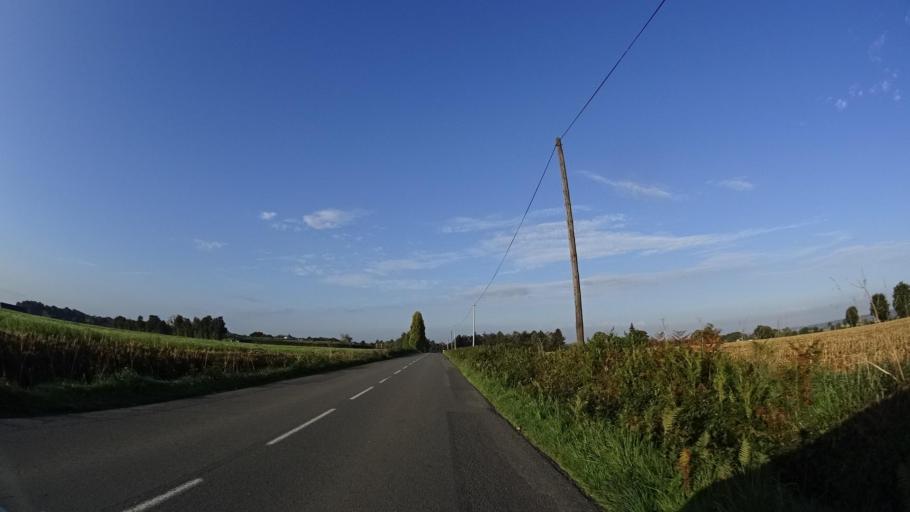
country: FR
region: Brittany
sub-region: Departement d'Ille-et-Vilaine
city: Quedillac
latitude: 48.2328
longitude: -2.1702
